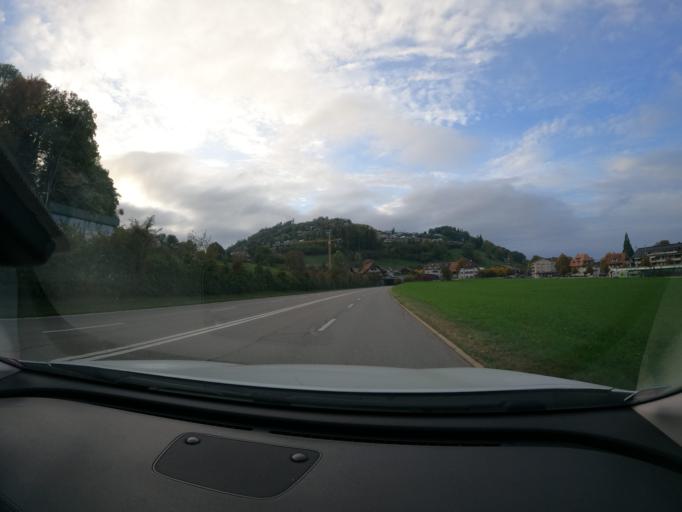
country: CH
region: Bern
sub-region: Bern-Mittelland District
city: Kehrsatz
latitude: 46.9078
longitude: 7.4720
